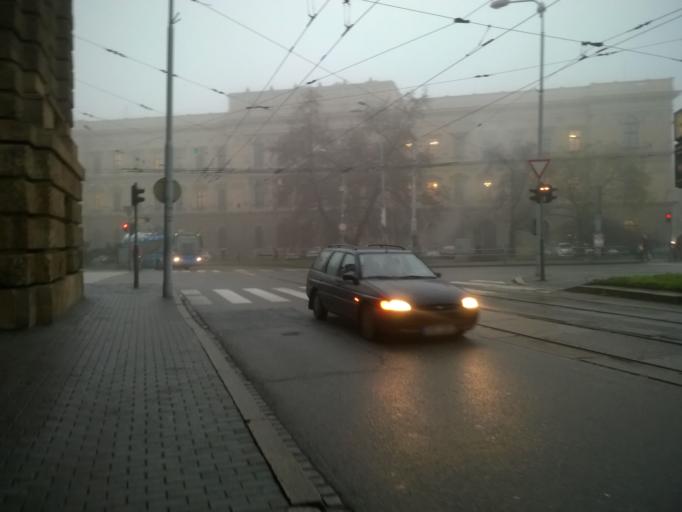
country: CZ
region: South Moravian
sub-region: Mesto Brno
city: Brno
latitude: 49.1985
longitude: 16.6034
